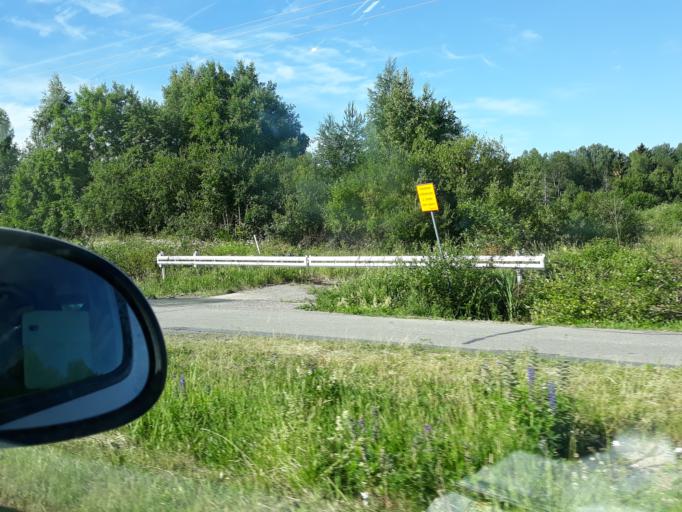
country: FI
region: Uusimaa
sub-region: Helsinki
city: Jaervenpaeae
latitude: 60.5445
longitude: 24.9860
